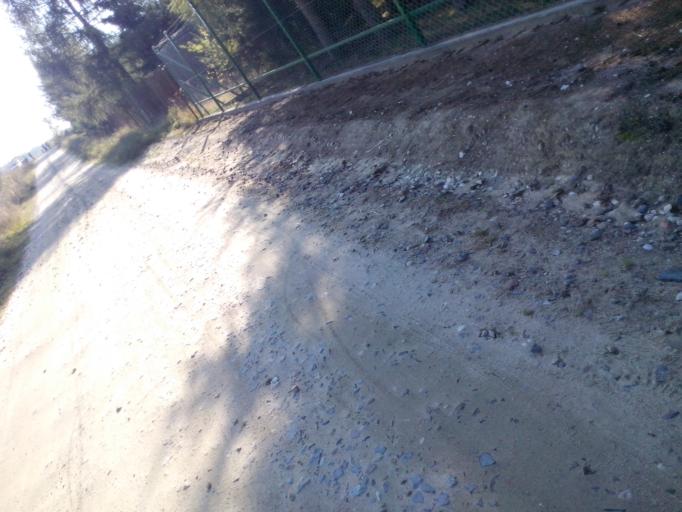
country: PL
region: Kujawsko-Pomorskie
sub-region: Powiat brodnicki
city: Gorzno
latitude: 53.2005
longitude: 19.6573
